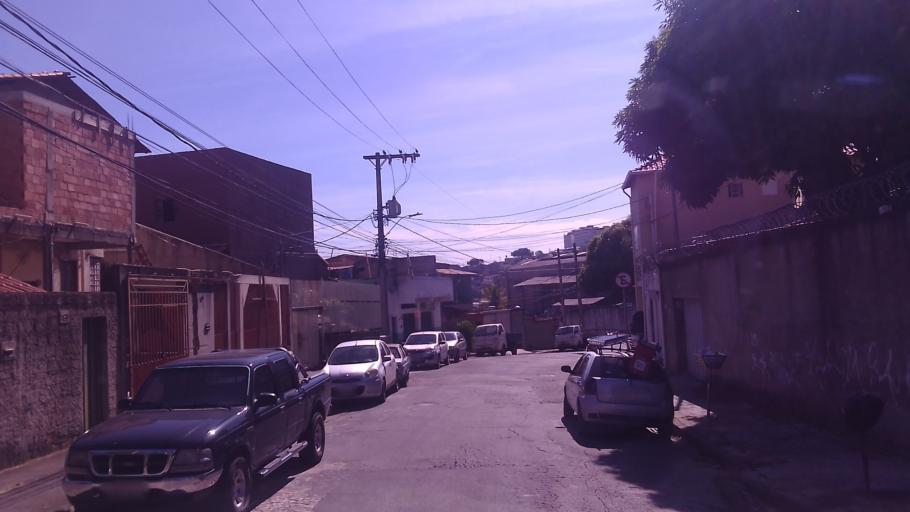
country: BR
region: Minas Gerais
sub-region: Contagem
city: Contagem
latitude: -19.9183
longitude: -44.0005
